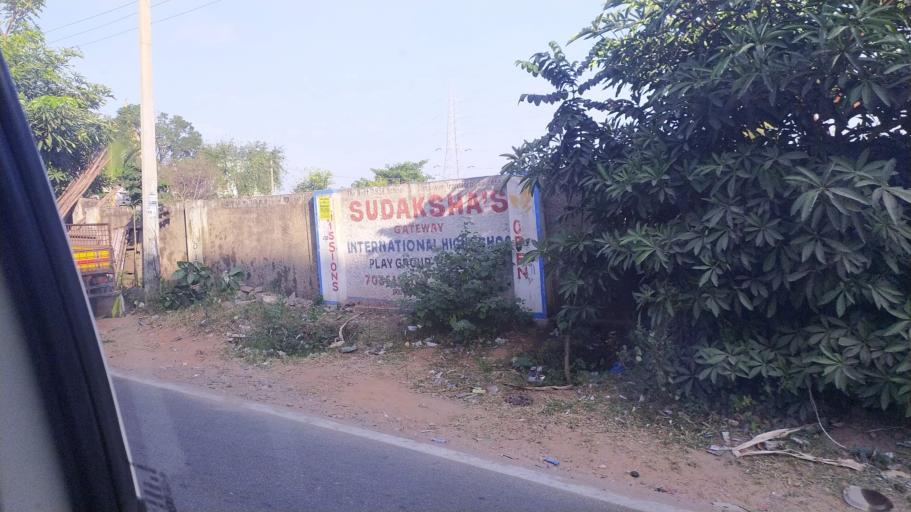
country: IN
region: Telangana
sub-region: Hyderabad
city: Hyderabad
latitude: 17.3272
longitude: 78.4220
